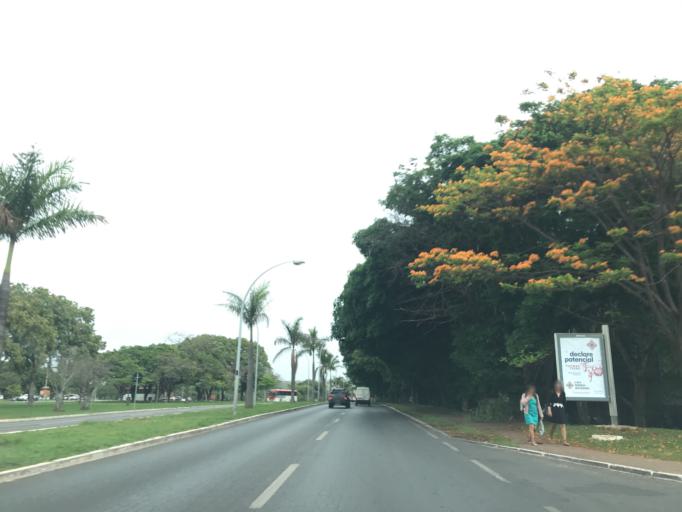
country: BR
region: Federal District
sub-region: Brasilia
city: Brasilia
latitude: -15.7423
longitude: -47.8897
